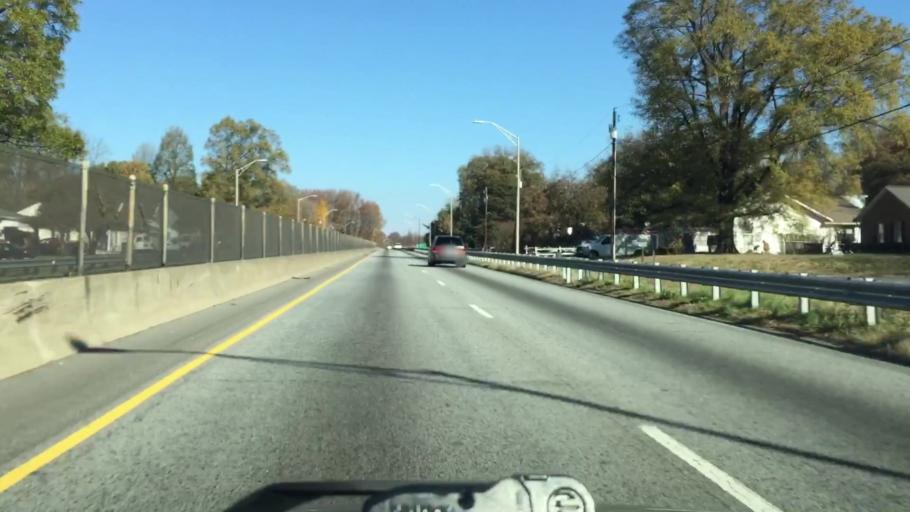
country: US
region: North Carolina
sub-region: Guilford County
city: Greensboro
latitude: 36.0943
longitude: -79.7656
